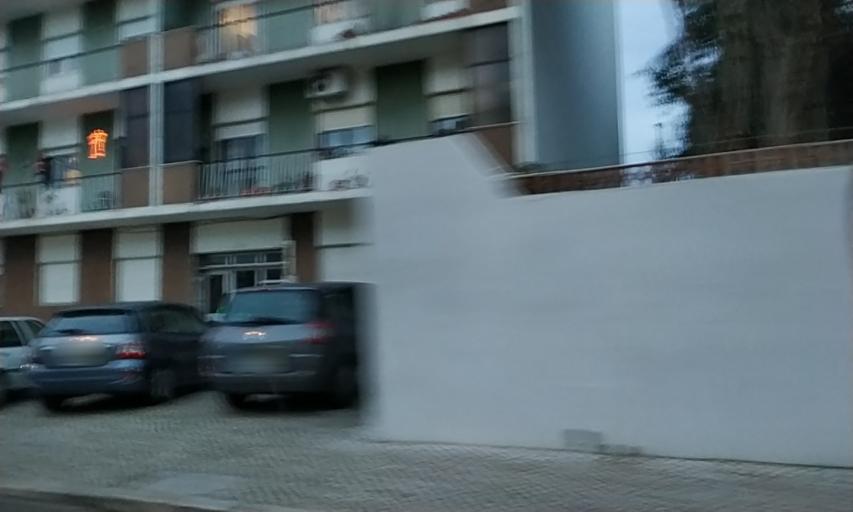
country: PT
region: Setubal
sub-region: Setubal
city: Setubal
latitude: 38.5247
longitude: -8.8750
